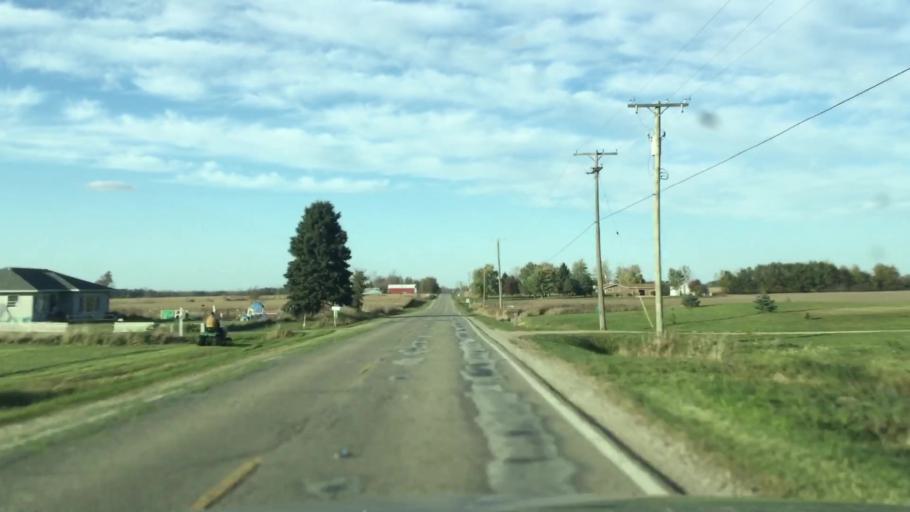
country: US
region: Michigan
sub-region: Lapeer County
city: North Branch
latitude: 43.2696
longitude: -83.1981
